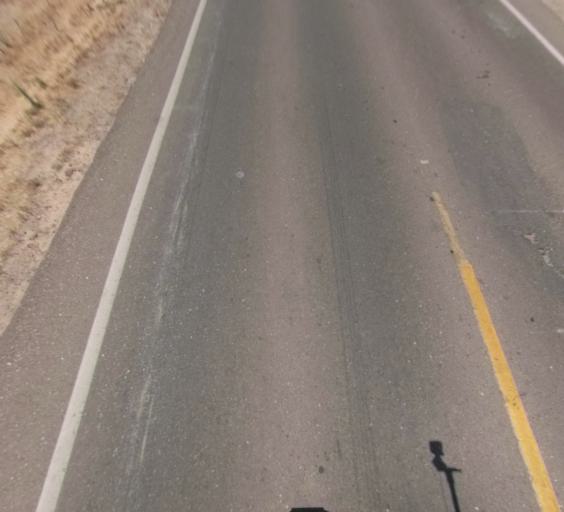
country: US
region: California
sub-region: Madera County
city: Madera Acres
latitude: 36.9948
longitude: -120.0286
